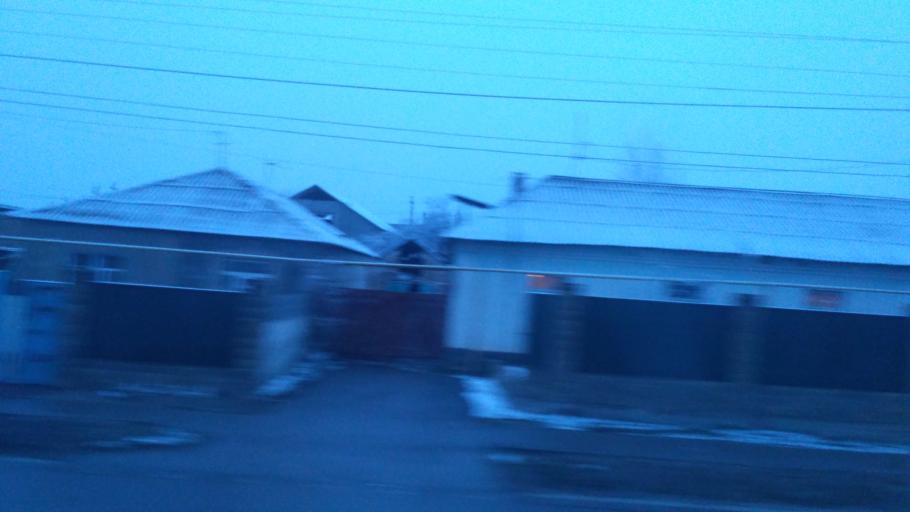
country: KZ
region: Ongtustik Qazaqstan
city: Shymkent
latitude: 42.3692
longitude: 69.5091
